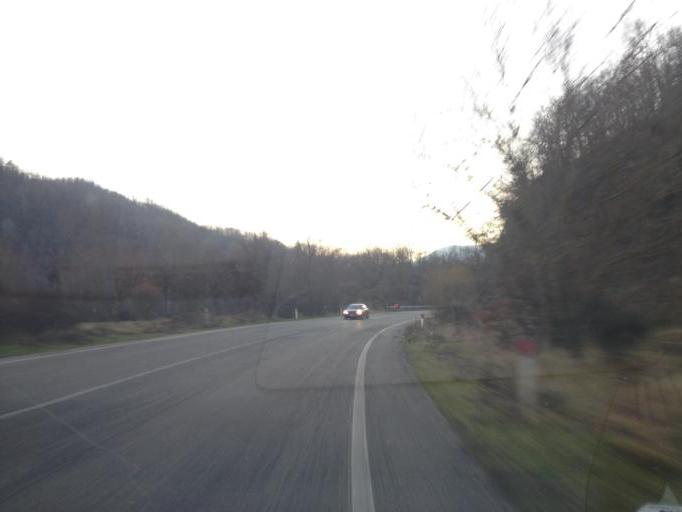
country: IT
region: The Marches
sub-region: Provincia di Ascoli Piceno
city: Arquata del Tronto
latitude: 42.7562
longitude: 13.2819
